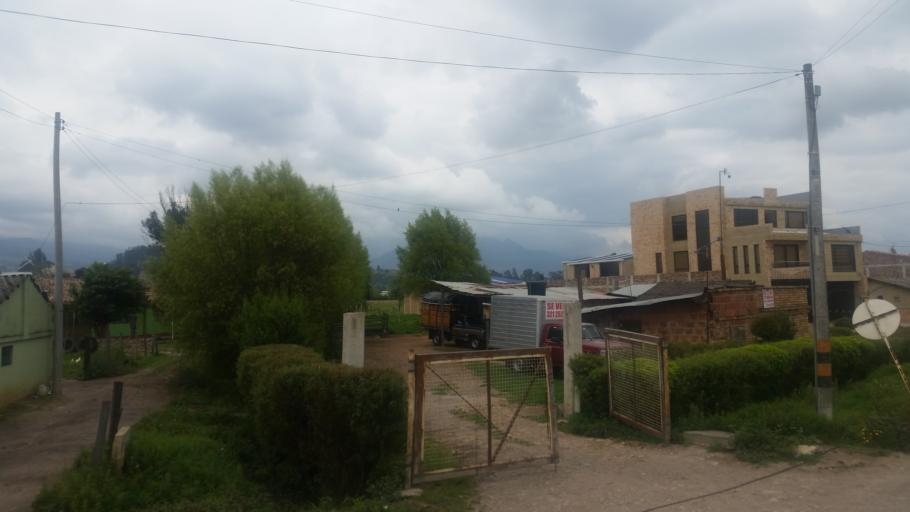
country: CO
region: Cundinamarca
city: Cogua
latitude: 5.0352
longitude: -73.9653
